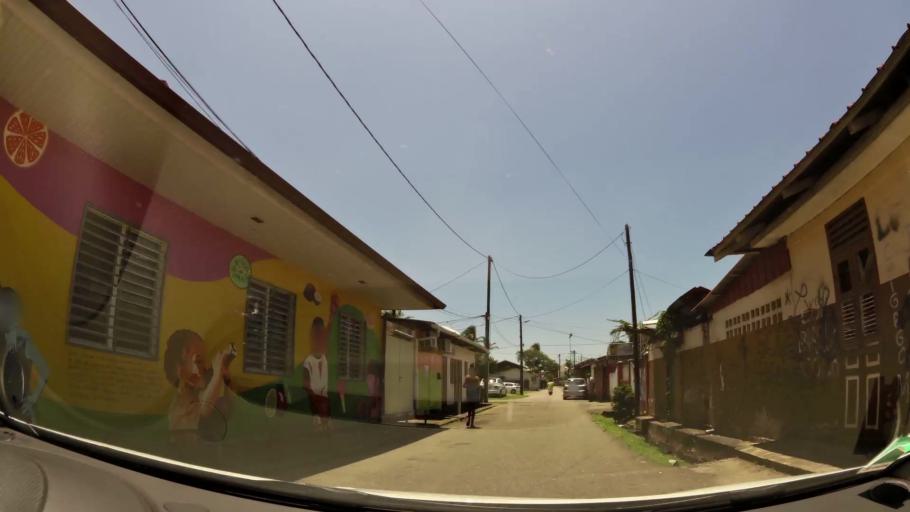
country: GF
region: Guyane
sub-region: Guyane
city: Cayenne
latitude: 4.9329
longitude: -52.3338
